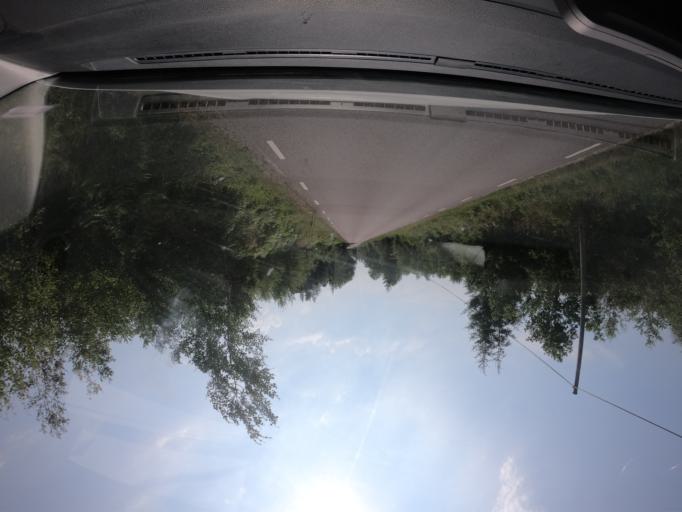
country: SE
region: Skane
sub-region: Hassleholms Kommun
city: Bjarnum
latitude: 56.3340
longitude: 13.6247
